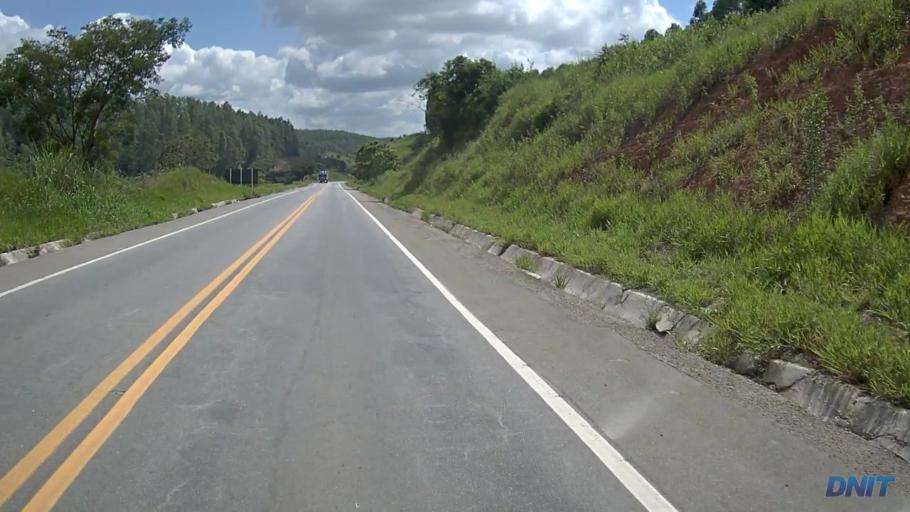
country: BR
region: Minas Gerais
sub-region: Governador Valadares
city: Governador Valadares
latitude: -19.0787
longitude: -42.1808
